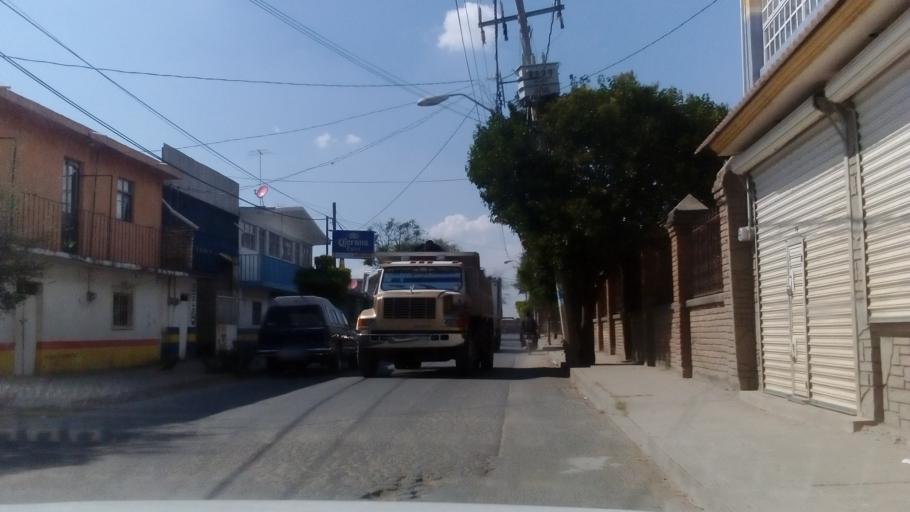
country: MX
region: Guanajuato
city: Duarte
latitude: 21.0879
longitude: -101.5261
